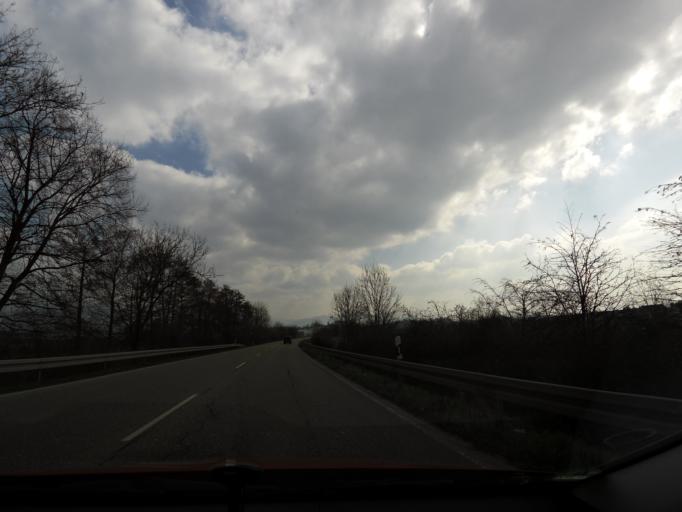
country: DE
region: Baden-Wuerttemberg
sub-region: Freiburg Region
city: Achern
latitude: 48.6367
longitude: 8.0464
